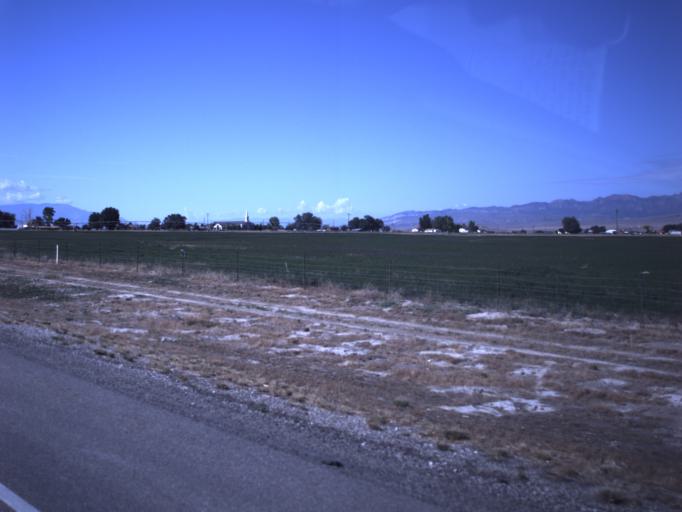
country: US
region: Utah
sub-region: Sanpete County
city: Centerfield
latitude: 39.0612
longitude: -111.8208
